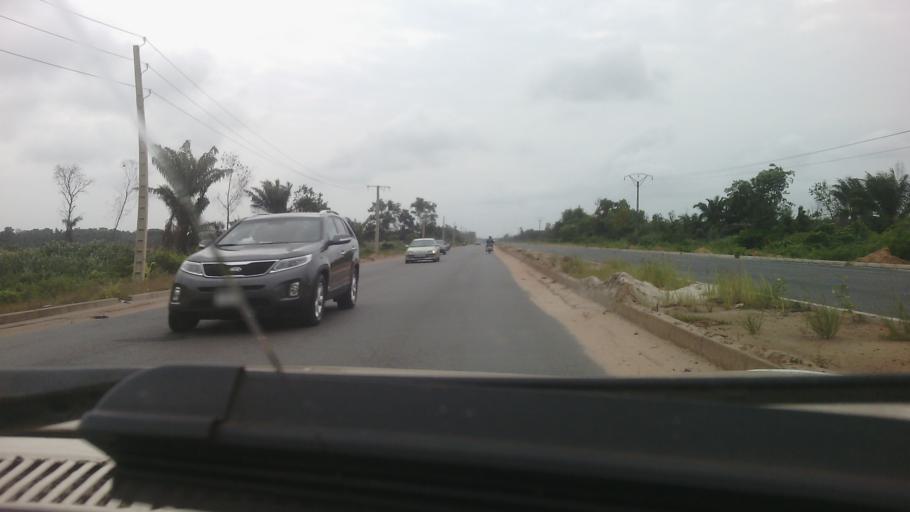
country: BJ
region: Atlantique
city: Ouidah
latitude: 6.3746
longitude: 2.1488
